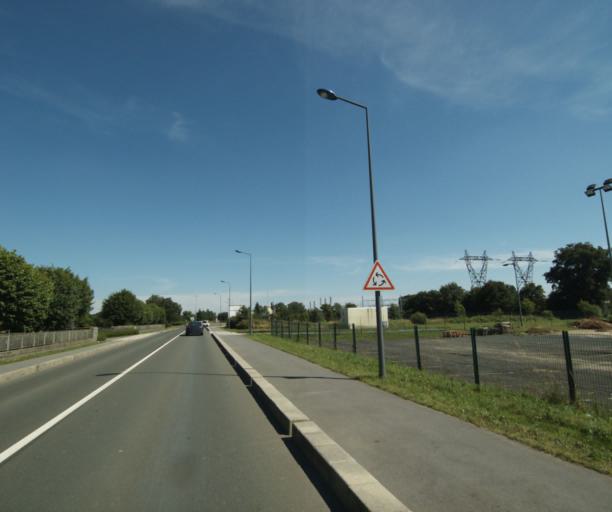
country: FR
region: Pays de la Loire
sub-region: Departement de la Mayenne
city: Laval
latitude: 48.0535
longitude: -0.7956
